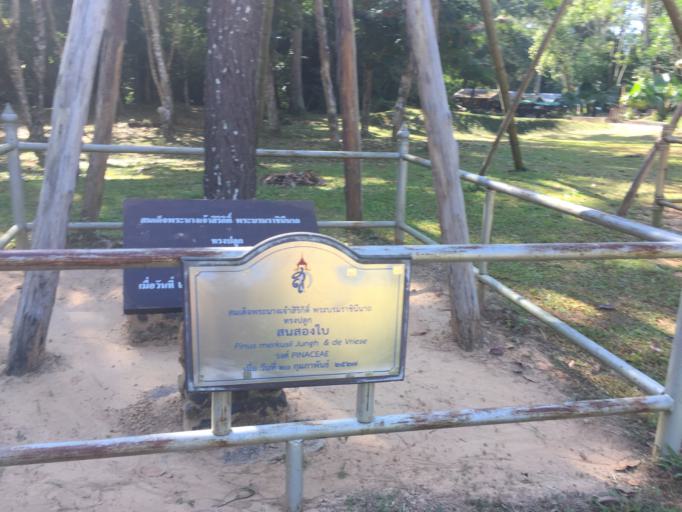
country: TH
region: Phetchabun
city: Khao Kho
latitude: 16.6296
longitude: 100.9404
